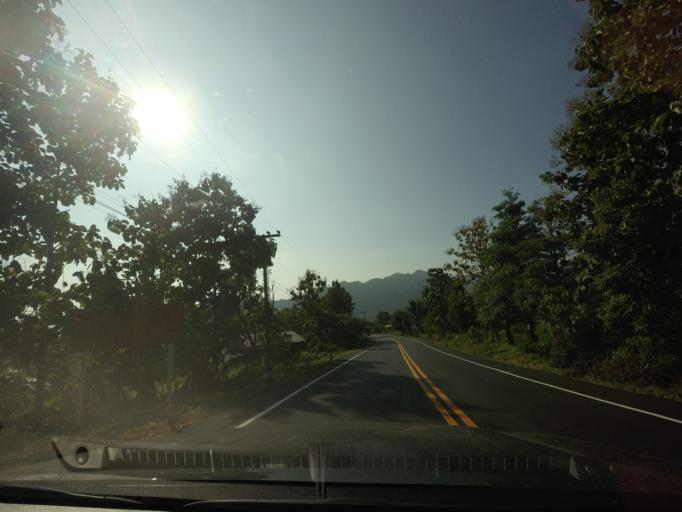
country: TH
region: Phetchabun
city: Lom Kao
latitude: 16.8753
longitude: 101.1301
